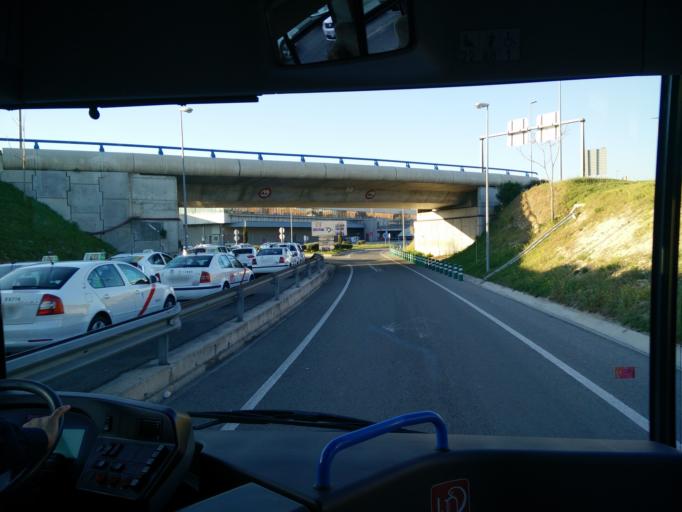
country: ES
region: Madrid
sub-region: Provincia de Madrid
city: Barajas de Madrid
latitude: 40.4631
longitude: -3.5748
